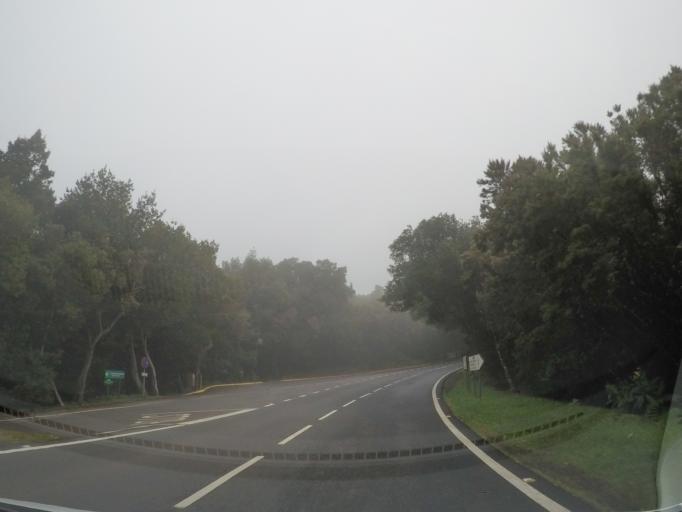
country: ES
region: Canary Islands
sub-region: Provincia de Santa Cruz de Tenerife
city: Vallehermosa
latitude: 28.1274
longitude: -17.2562
